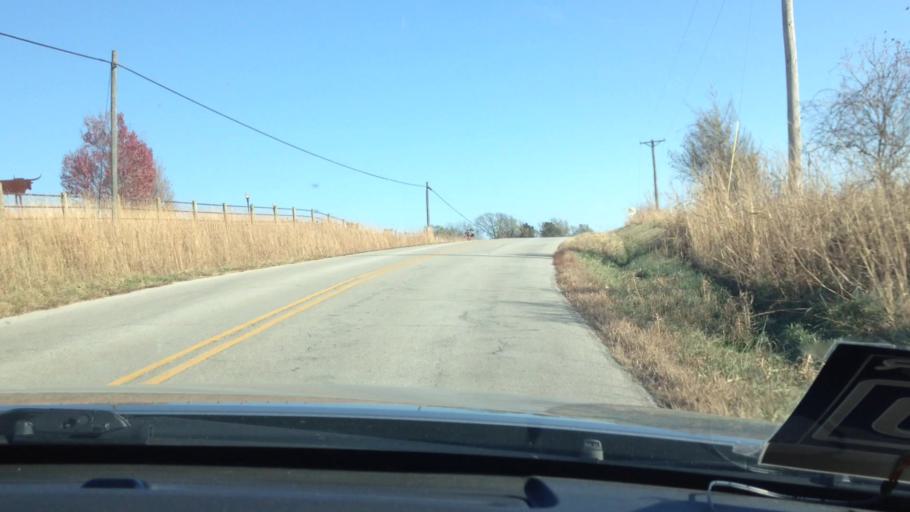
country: US
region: Missouri
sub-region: Platte County
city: Weston
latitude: 39.4278
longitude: -94.8655
